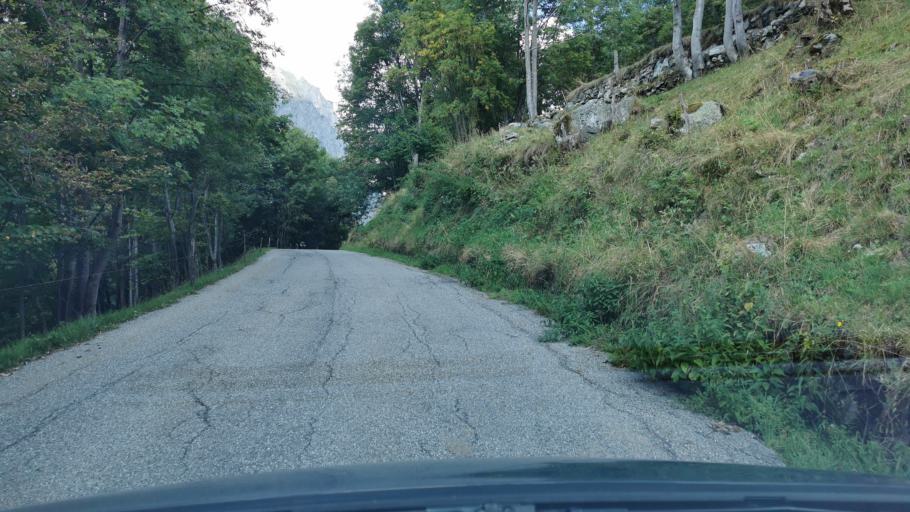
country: IT
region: Piedmont
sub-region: Provincia di Torino
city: Usseglio
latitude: 45.2256
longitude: 7.2031
